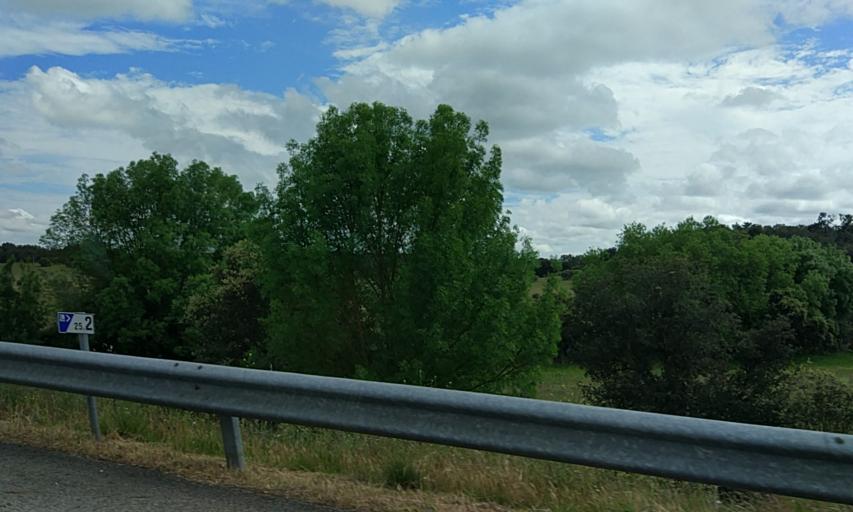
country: PT
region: Evora
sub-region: Vendas Novas
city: Vendas Novas
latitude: 38.6442
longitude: -8.3703
